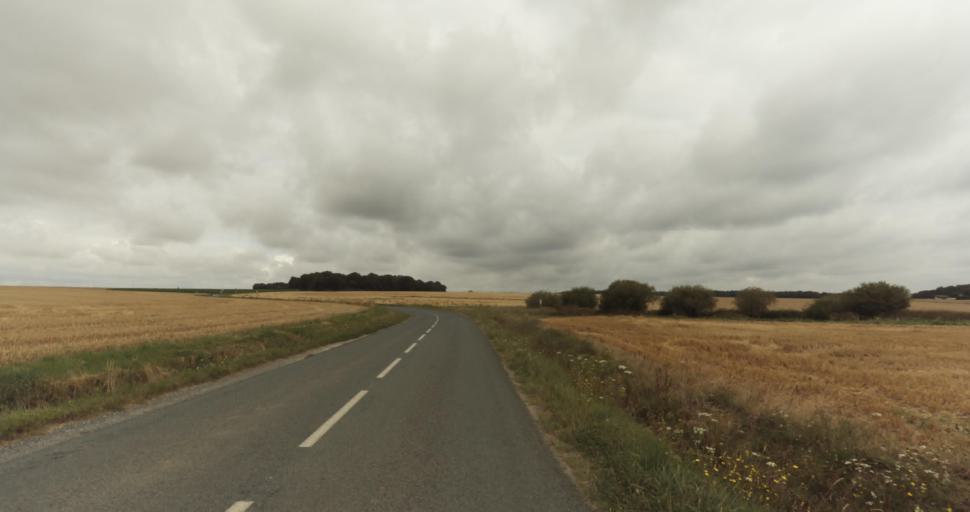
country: FR
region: Haute-Normandie
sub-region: Departement de l'Eure
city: La Couture-Boussey
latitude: 48.9352
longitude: 1.3917
